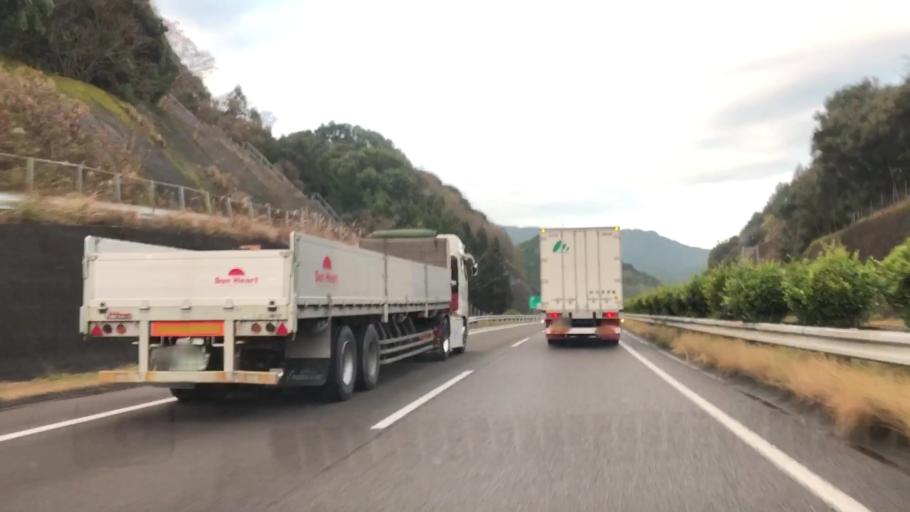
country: JP
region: Saga Prefecture
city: Takeocho-takeo
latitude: 33.1635
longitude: 130.0306
